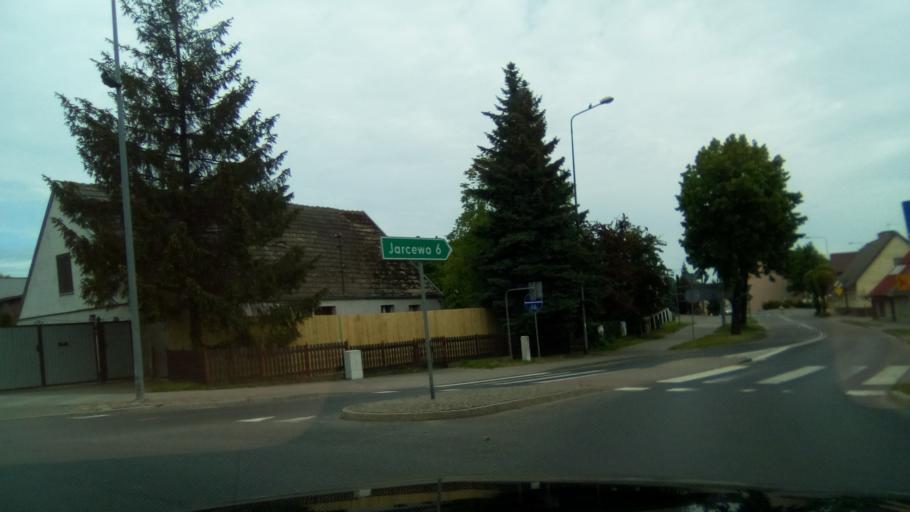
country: PL
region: Pomeranian Voivodeship
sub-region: Powiat chojnicki
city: Chojnice
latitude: 53.6988
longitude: 17.5567
